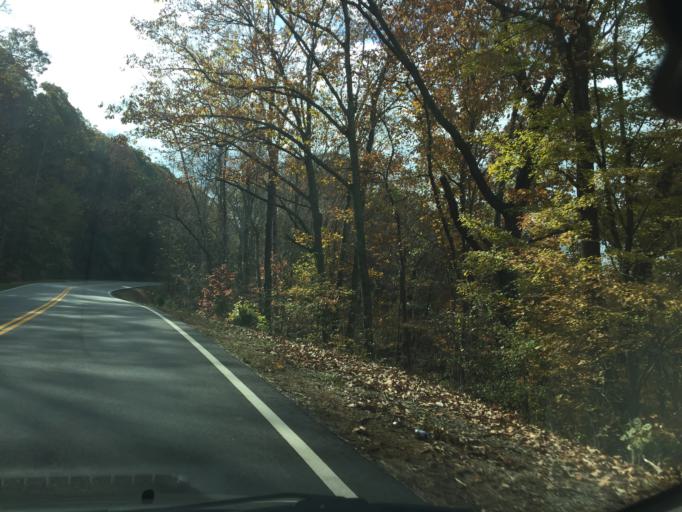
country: US
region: Georgia
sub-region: Dade County
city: Trenton
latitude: 34.8482
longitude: -85.4990
